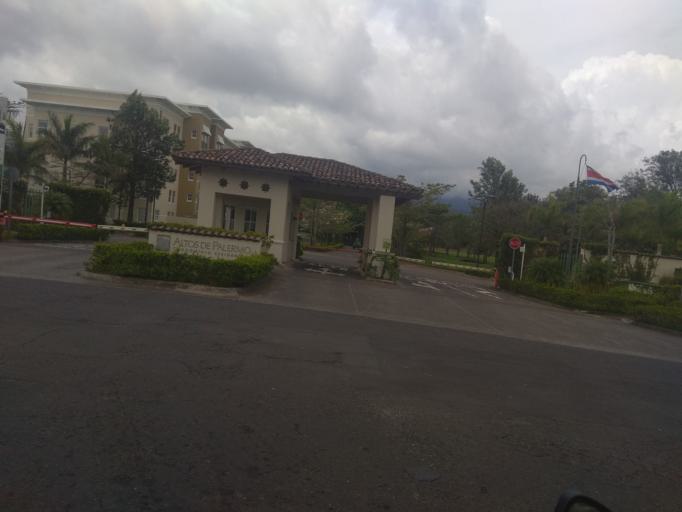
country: CR
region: Heredia
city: San Pablo
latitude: 10.0030
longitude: -84.1007
